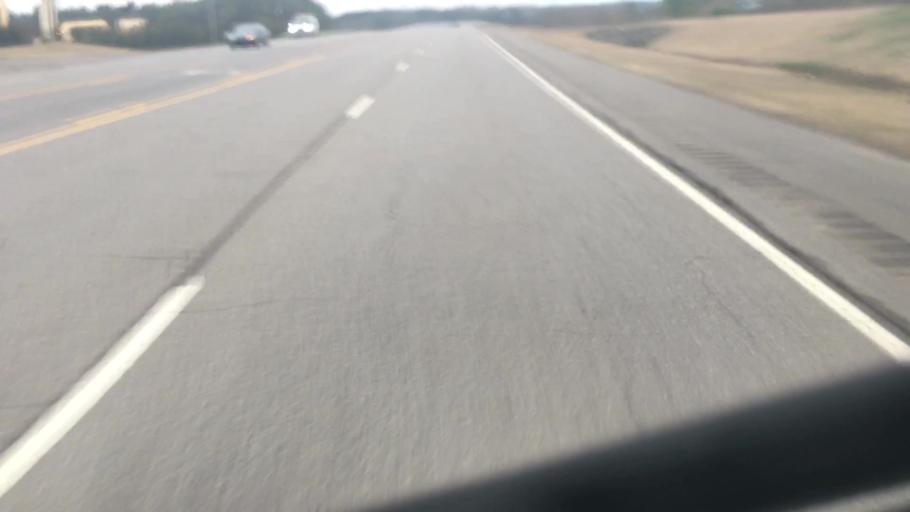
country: US
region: Alabama
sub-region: Walker County
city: Jasper
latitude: 33.8116
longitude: -87.2337
